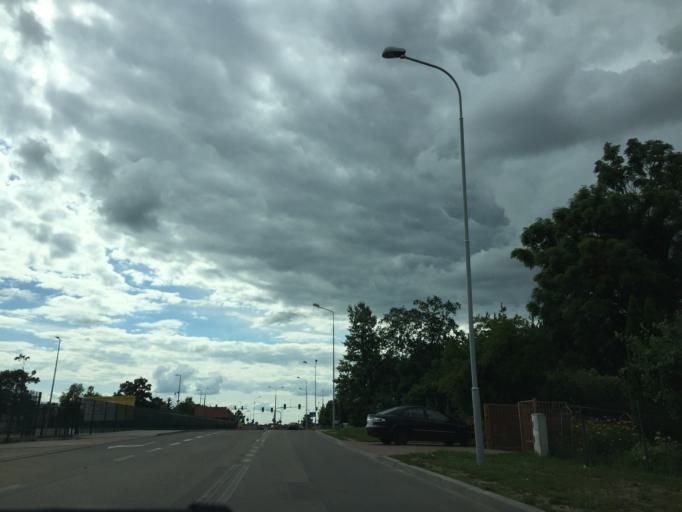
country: PL
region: Podlasie
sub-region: Suwalki
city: Suwalki
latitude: 54.0890
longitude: 22.9323
